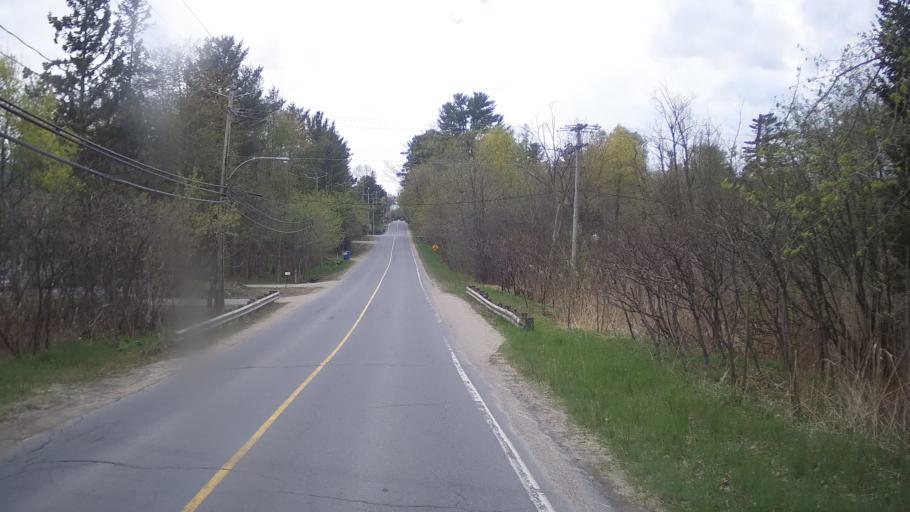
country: CA
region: Quebec
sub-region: Monteregie
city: Hudson
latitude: 45.4526
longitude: -74.1622
